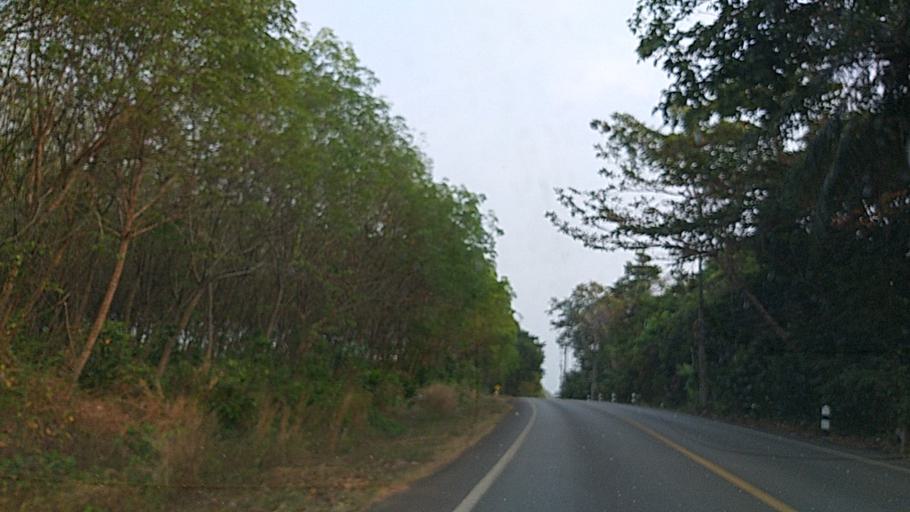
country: TH
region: Trat
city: Laem Ngop
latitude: 12.1949
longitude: 102.2891
